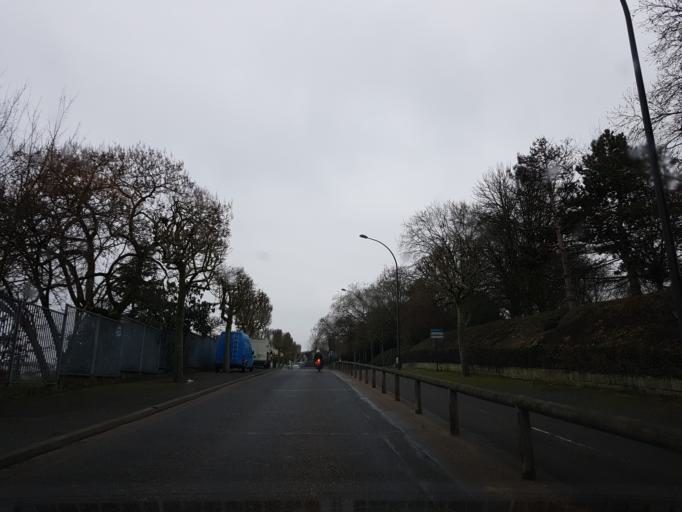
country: FR
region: Ile-de-France
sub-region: Departement du Val-de-Marne
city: Vitry-sur-Seine
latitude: 48.7803
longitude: 2.3909
